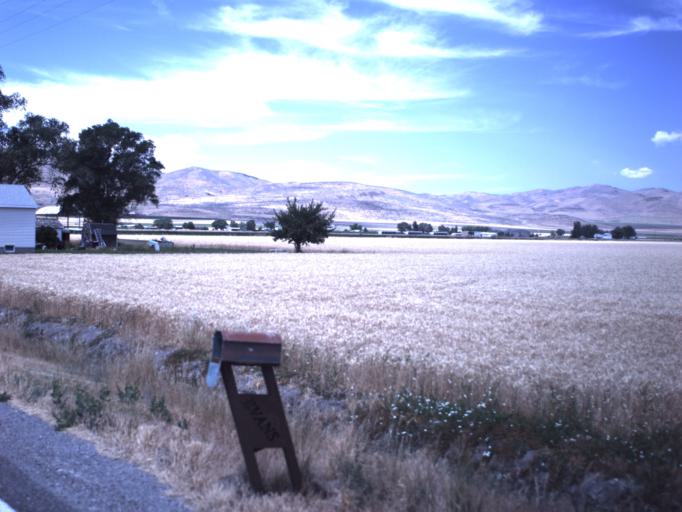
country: US
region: Utah
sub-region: Box Elder County
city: Tremonton
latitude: 41.7096
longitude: -112.2635
